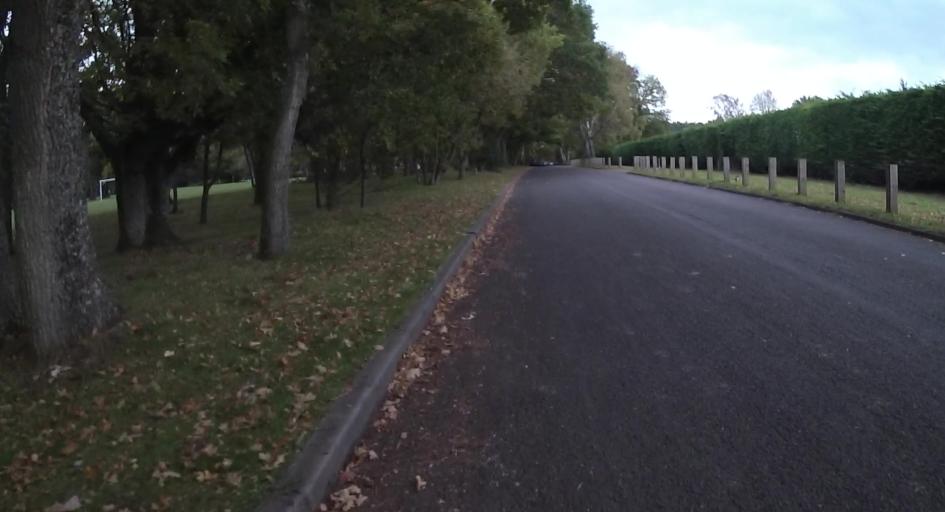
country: GB
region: England
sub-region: Bracknell Forest
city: Crowthorne
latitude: 51.3921
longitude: -0.7795
